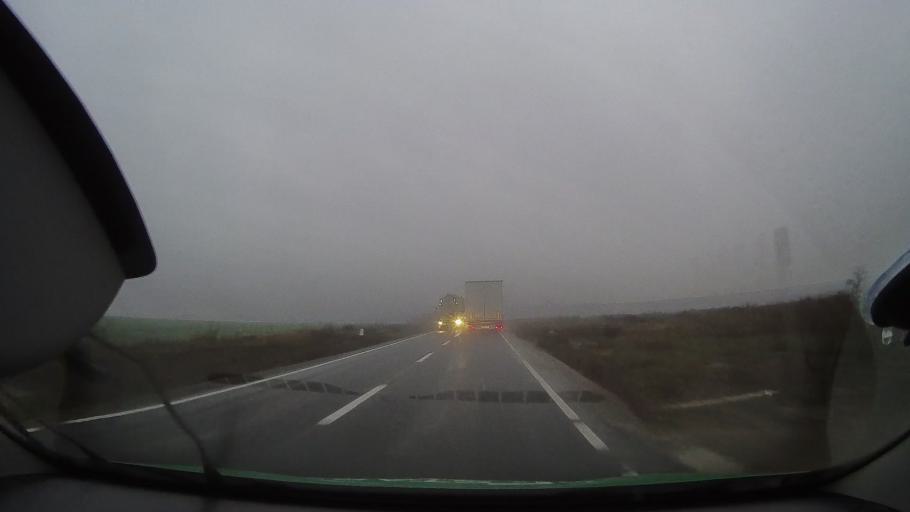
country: RO
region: Bihor
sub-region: Comuna Olcea
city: Calacea
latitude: 46.6520
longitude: 21.9590
